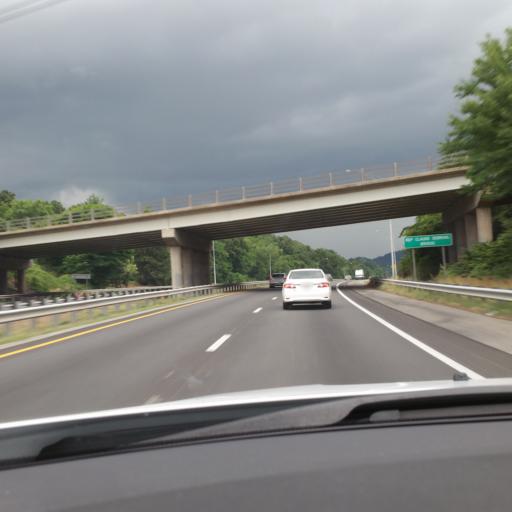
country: US
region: North Carolina
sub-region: Buncombe County
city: Woodfin
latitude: 35.6305
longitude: -82.5805
